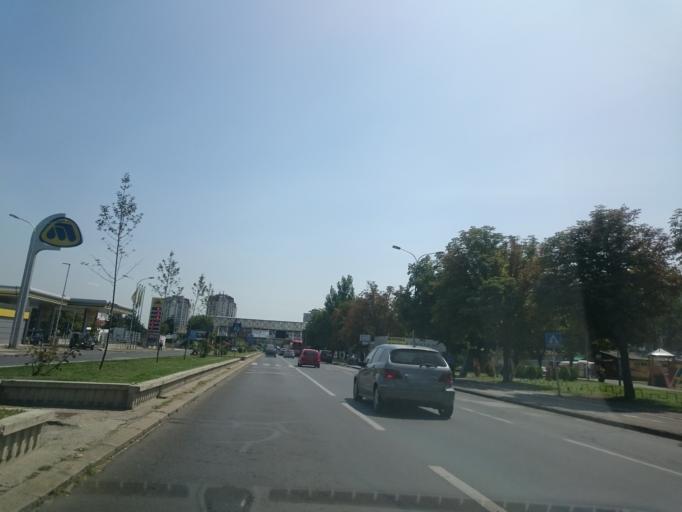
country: MK
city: Krushopek
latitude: 42.0073
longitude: 21.3735
